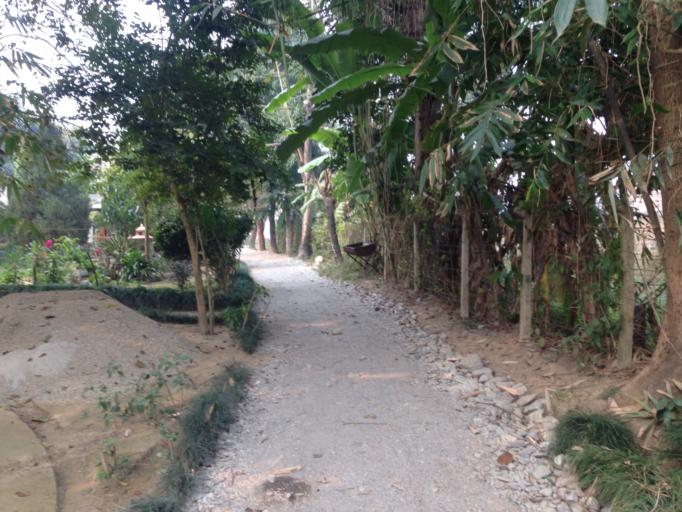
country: NP
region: Central Region
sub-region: Narayani Zone
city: Bharatpur
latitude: 27.5787
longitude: 84.4935
